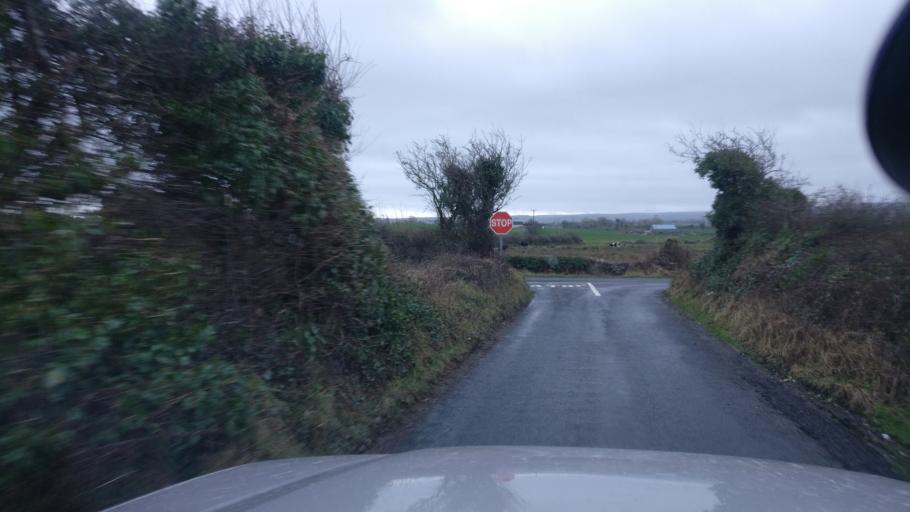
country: IE
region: Connaught
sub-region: County Galway
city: Loughrea
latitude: 53.2036
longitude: -8.6608
